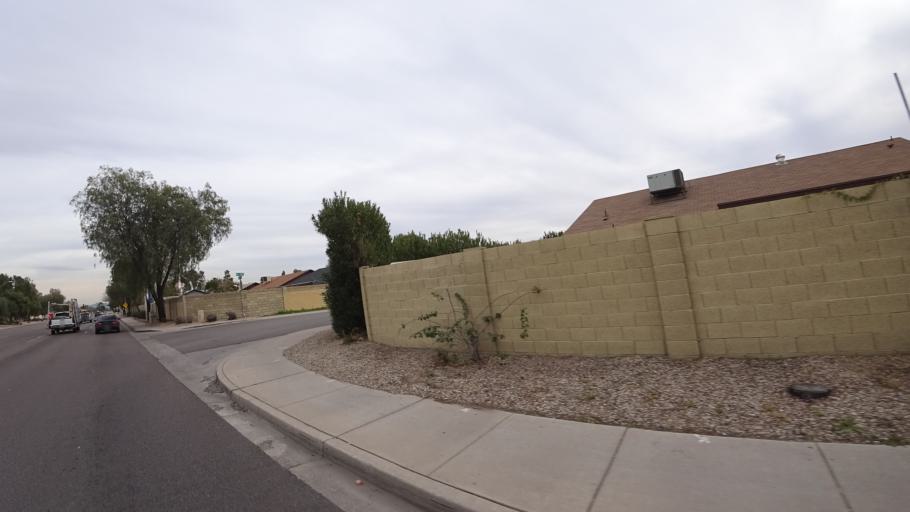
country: US
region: Arizona
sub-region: Maricopa County
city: Peoria
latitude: 33.5817
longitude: -112.1979
